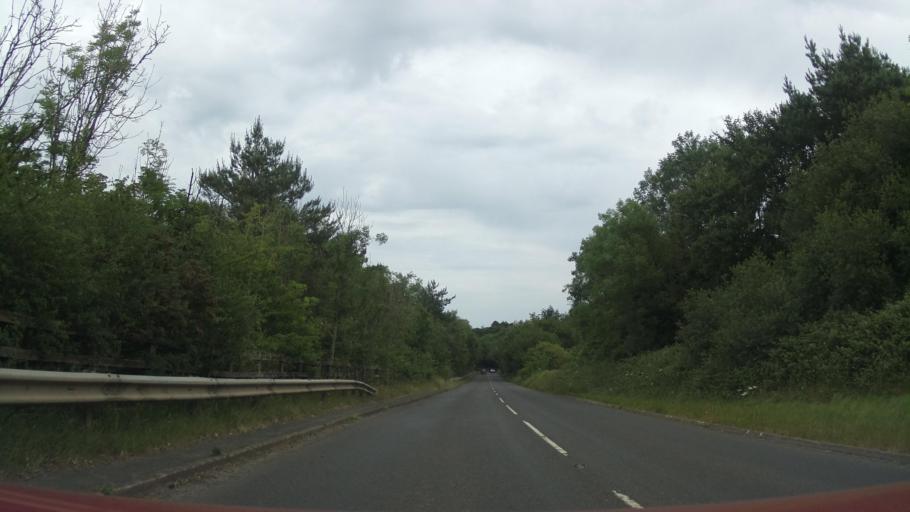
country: GB
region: England
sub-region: Devon
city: Bovey Tracey
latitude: 50.5517
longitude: -3.6815
